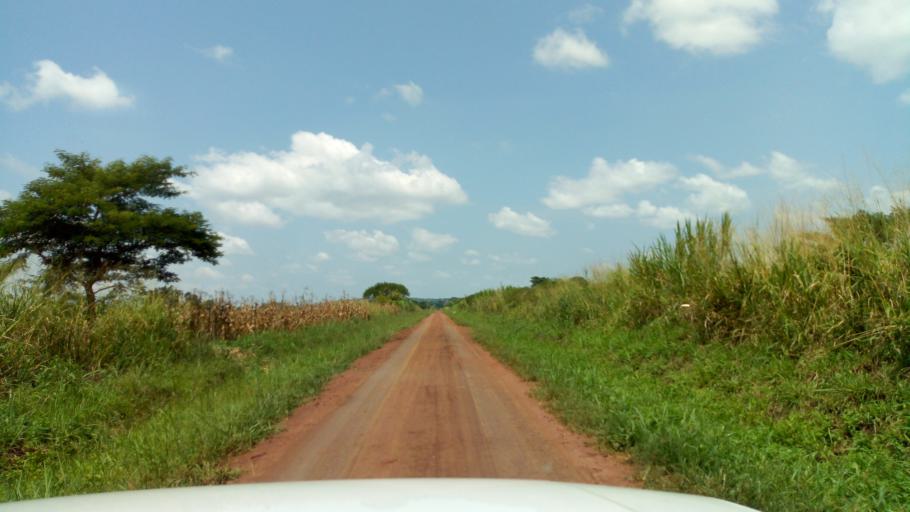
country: UG
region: Western Region
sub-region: Masindi District
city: Masindi
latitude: 1.7529
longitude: 31.8666
